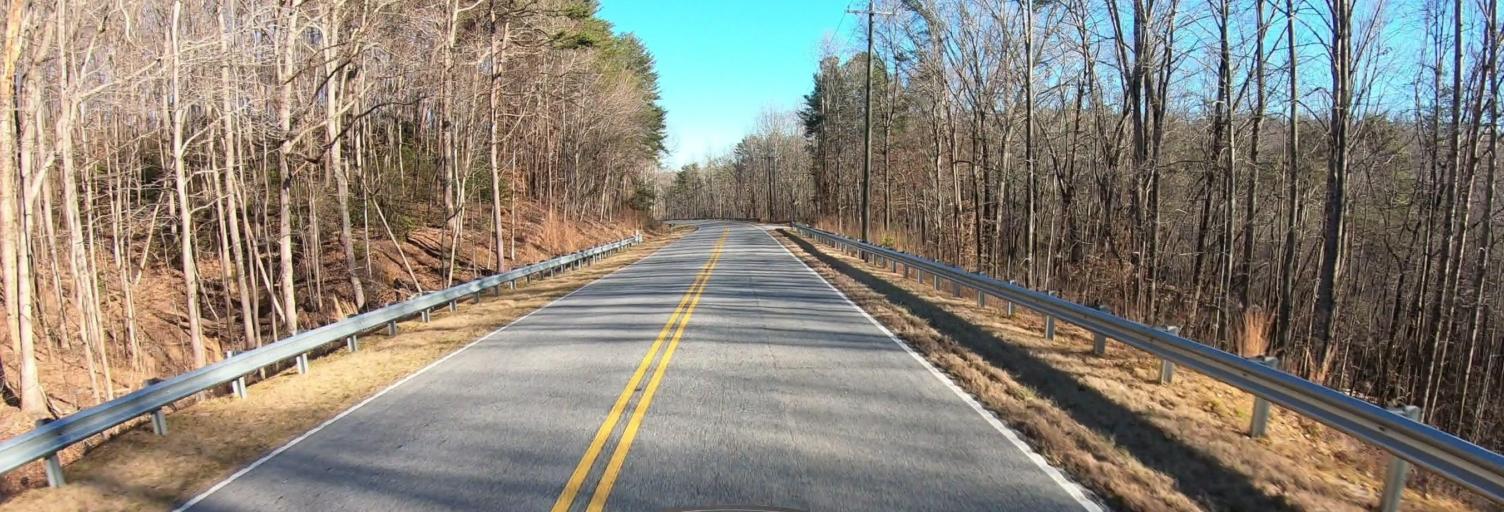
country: US
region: South Carolina
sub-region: Greenville County
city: Tigerville
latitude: 35.1035
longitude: -82.3795
